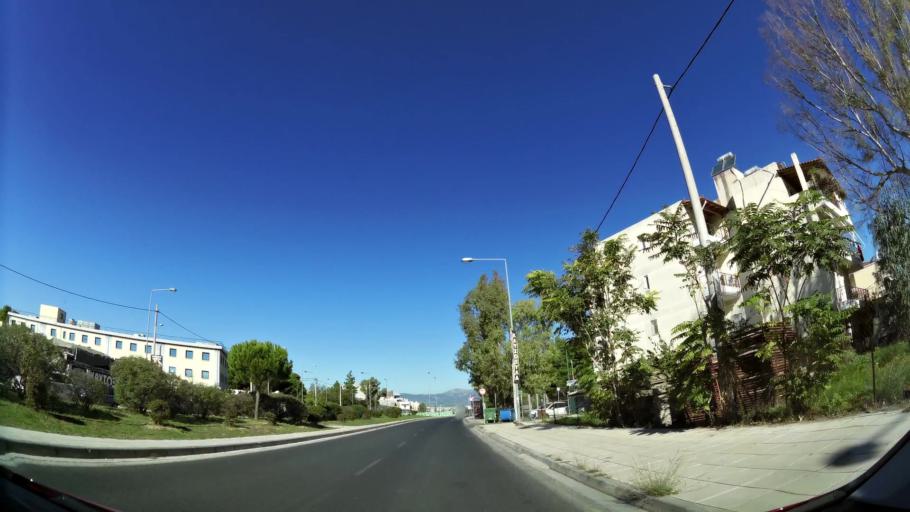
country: GR
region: Attica
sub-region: Nomarchia Athinas
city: Agia Paraskevi
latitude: 38.0165
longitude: 23.8410
